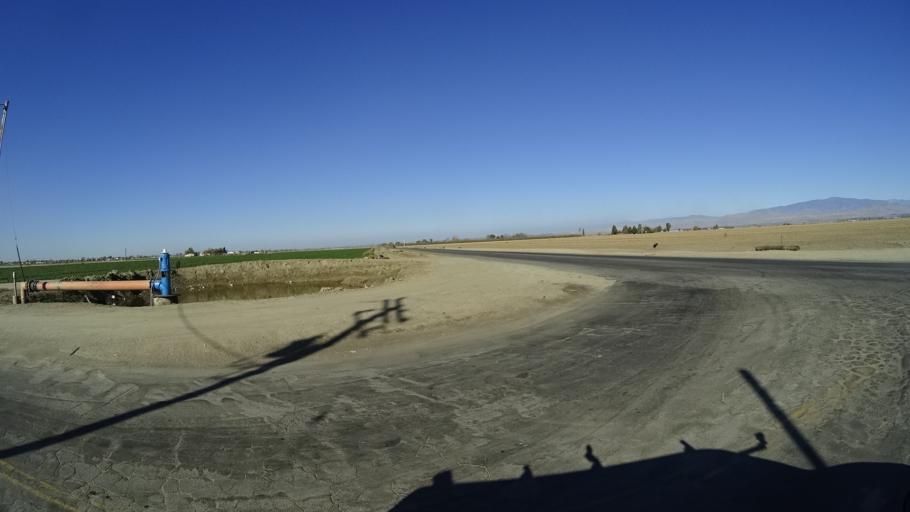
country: US
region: California
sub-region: Kern County
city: Greenfield
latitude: 35.2814
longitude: -118.9858
